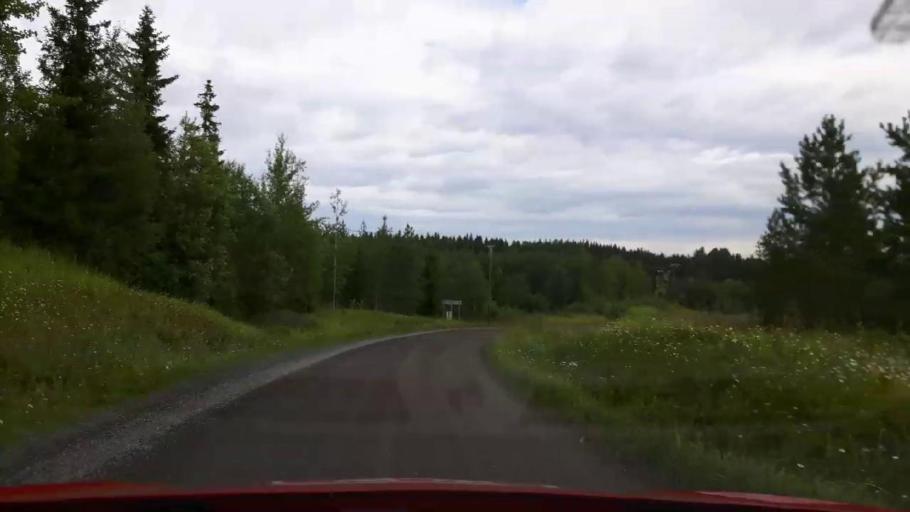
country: SE
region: Jaemtland
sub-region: Stroemsunds Kommun
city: Stroemsund
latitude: 63.4590
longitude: 15.2804
